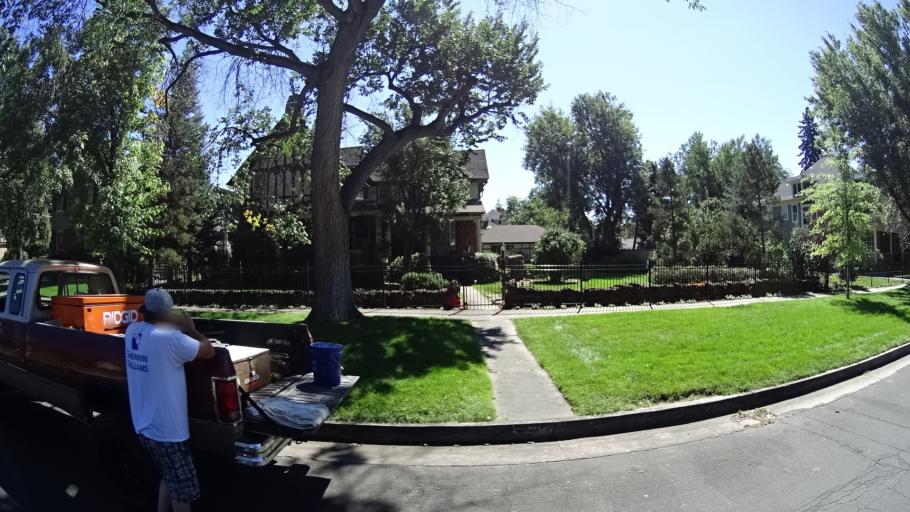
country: US
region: Colorado
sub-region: El Paso County
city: Colorado Springs
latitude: 38.8617
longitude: -104.8257
